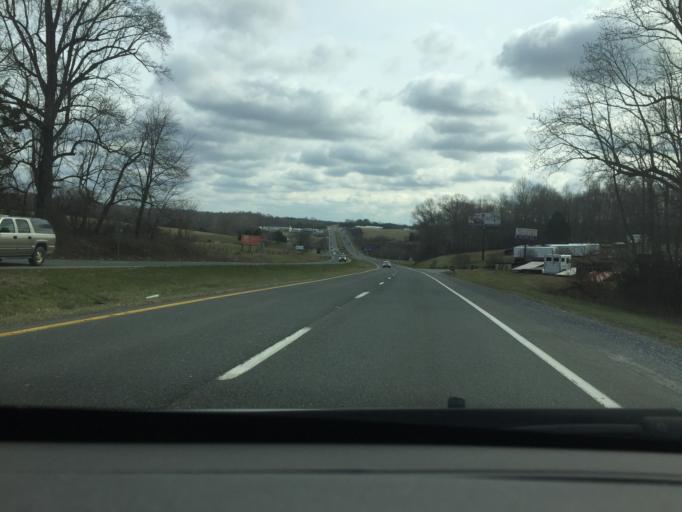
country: US
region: Virginia
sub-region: Campbell County
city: Timberlake
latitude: 37.3050
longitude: -79.2961
